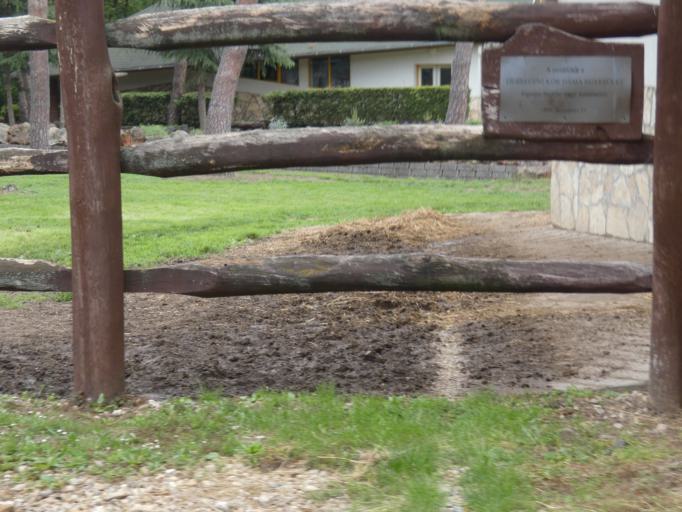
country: HU
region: Hajdu-Bihar
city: Debrecen
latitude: 47.5505
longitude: 21.6339
